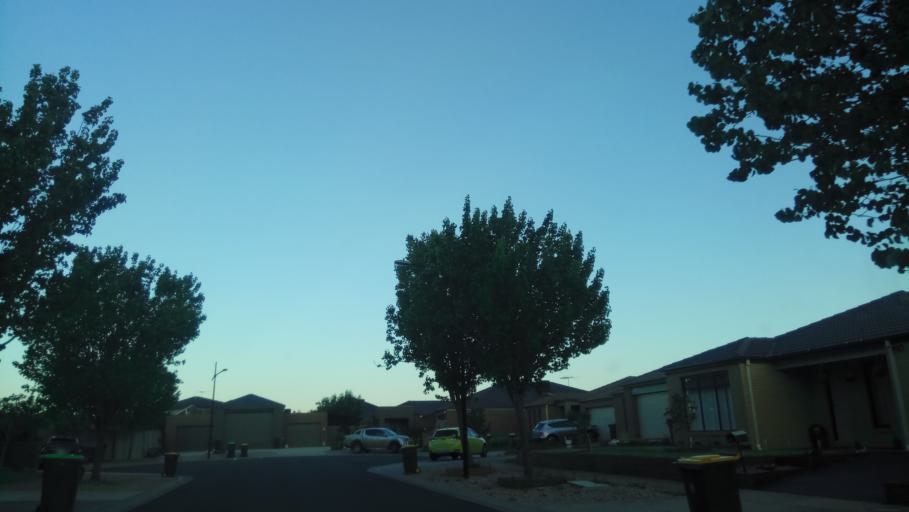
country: AU
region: Victoria
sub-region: Wyndham
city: Point Cook
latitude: -37.9013
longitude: 144.7464
